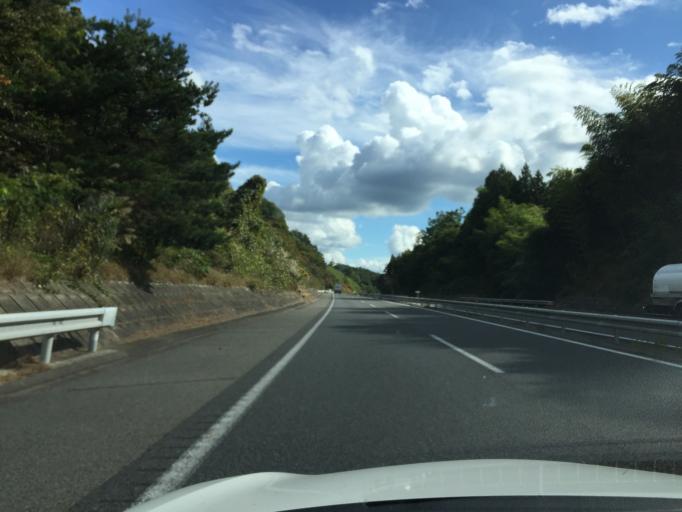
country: JP
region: Fukushima
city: Funehikimachi-funehiki
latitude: 37.3726
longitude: 140.6019
